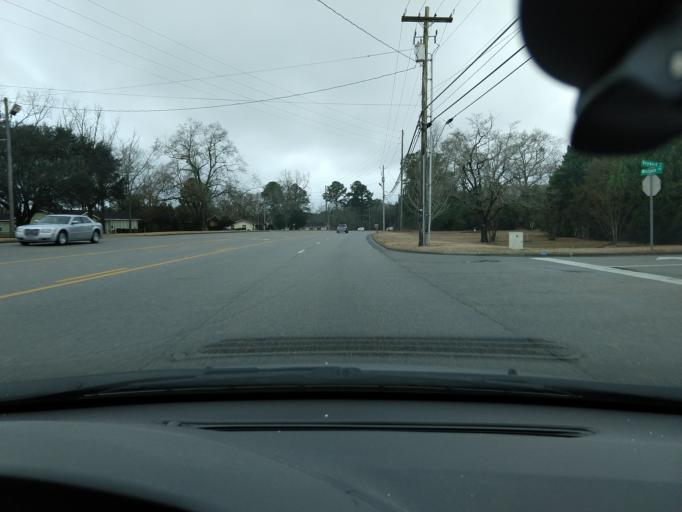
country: US
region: Alabama
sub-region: Houston County
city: Dothan
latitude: 31.2652
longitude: -85.4195
